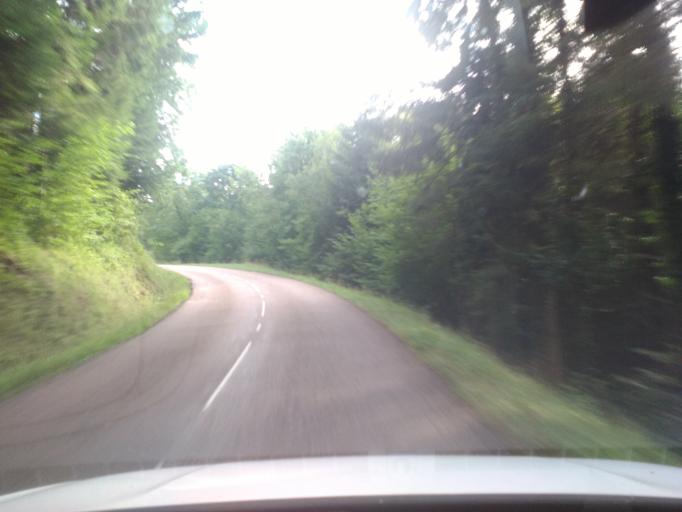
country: FR
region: Lorraine
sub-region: Departement des Vosges
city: Saint-Die-des-Vosges
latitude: 48.3302
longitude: 6.9836
